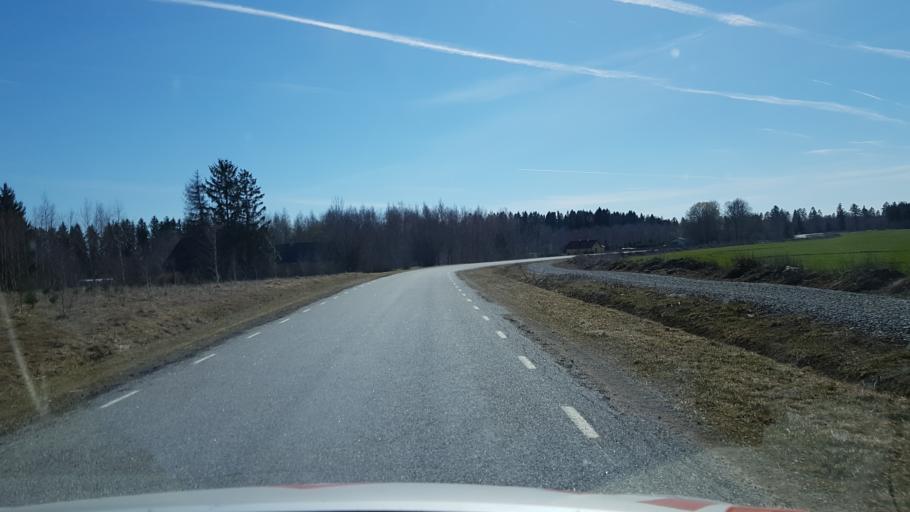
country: EE
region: Laeaene-Virumaa
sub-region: Viru-Nigula vald
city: Kunda
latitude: 59.3425
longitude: 26.6701
